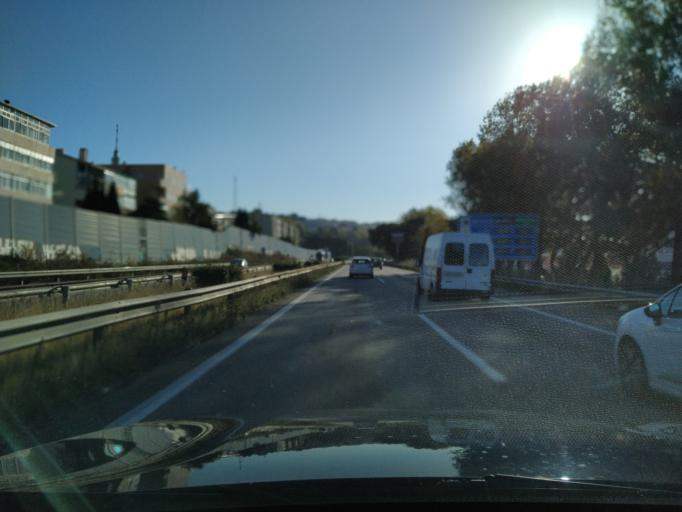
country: PT
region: Porto
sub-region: Vila Nova de Gaia
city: Vilar de Andorinho
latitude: 41.1120
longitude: -8.6124
